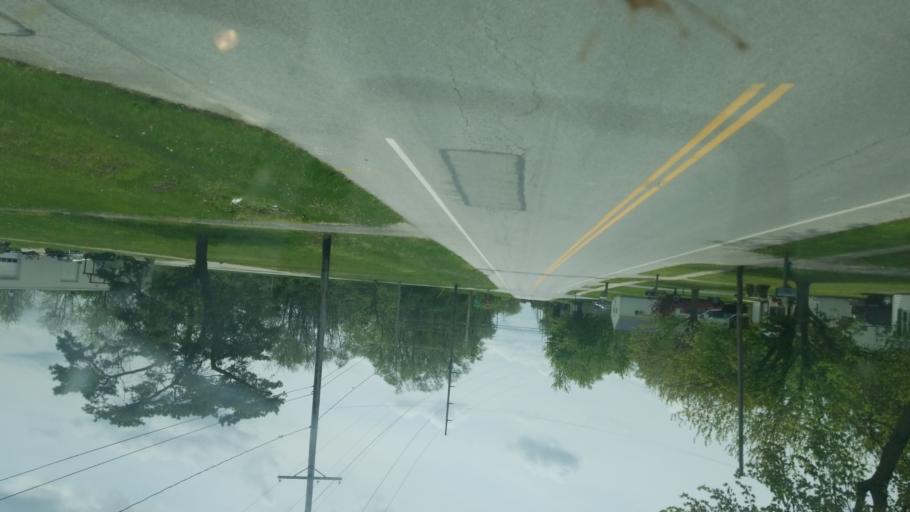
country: US
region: Ohio
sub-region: Sandusky County
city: Stony Prairie
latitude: 41.3504
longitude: -83.1463
